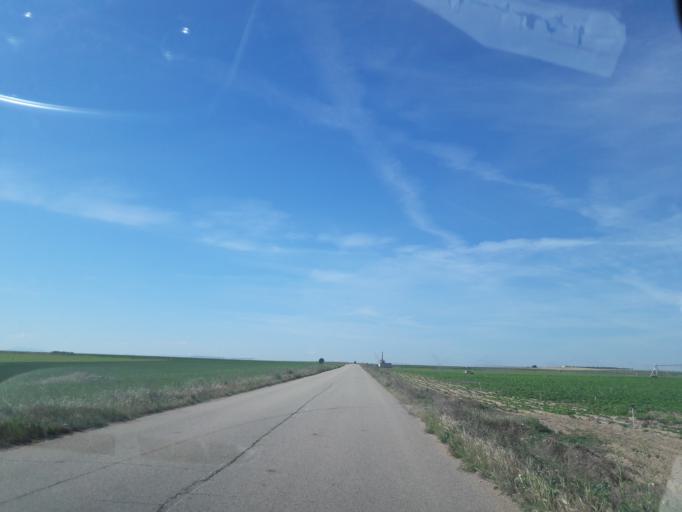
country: ES
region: Castille and Leon
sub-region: Provincia de Salamanca
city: Villoruela
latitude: 41.0312
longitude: -5.3910
